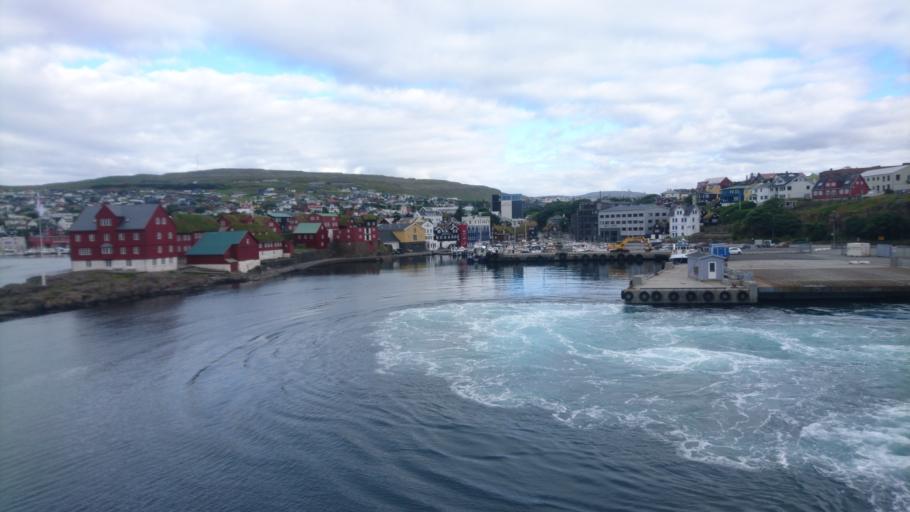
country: FO
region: Streymoy
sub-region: Torshavn
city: Torshavn
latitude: 62.0072
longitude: -6.7665
